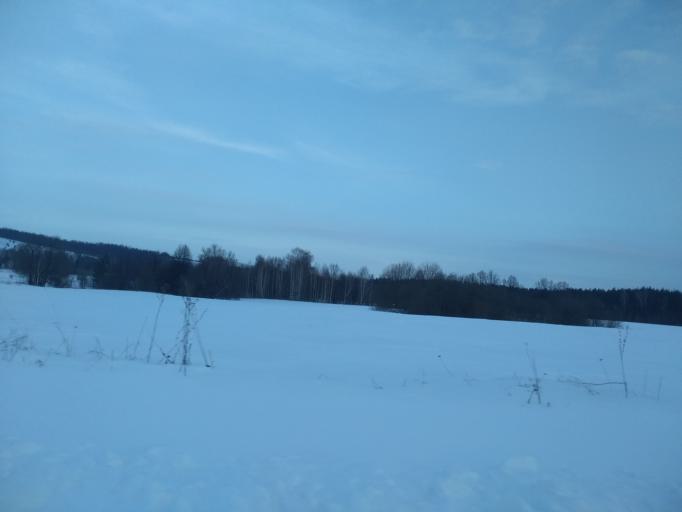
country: RU
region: Bashkortostan
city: Kudeyevskiy
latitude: 54.7155
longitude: 56.6311
